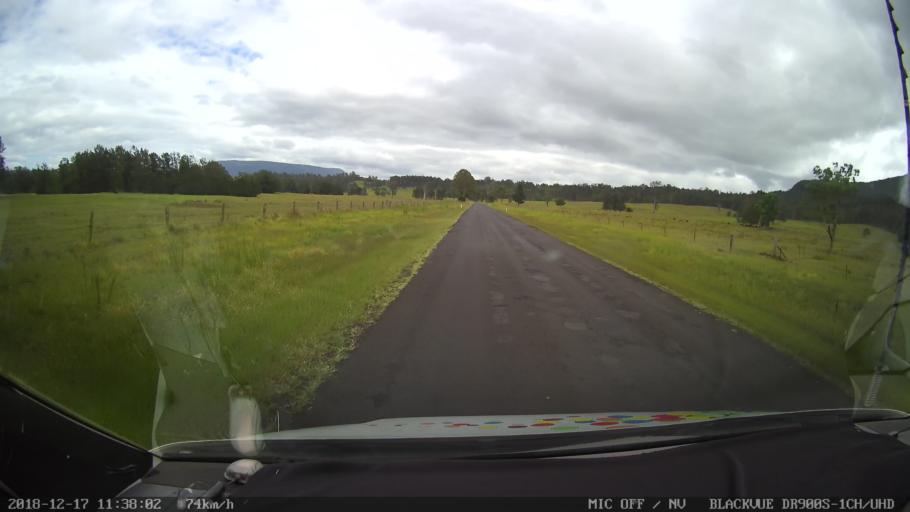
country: AU
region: New South Wales
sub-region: Kyogle
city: Kyogle
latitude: -28.6994
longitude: 152.6025
